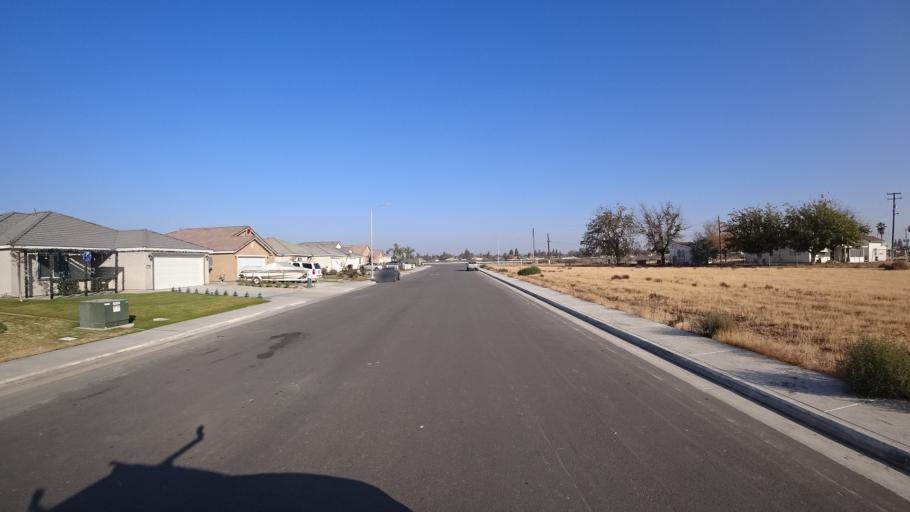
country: US
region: California
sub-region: Kern County
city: Greenfield
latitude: 35.2656
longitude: -119.0144
